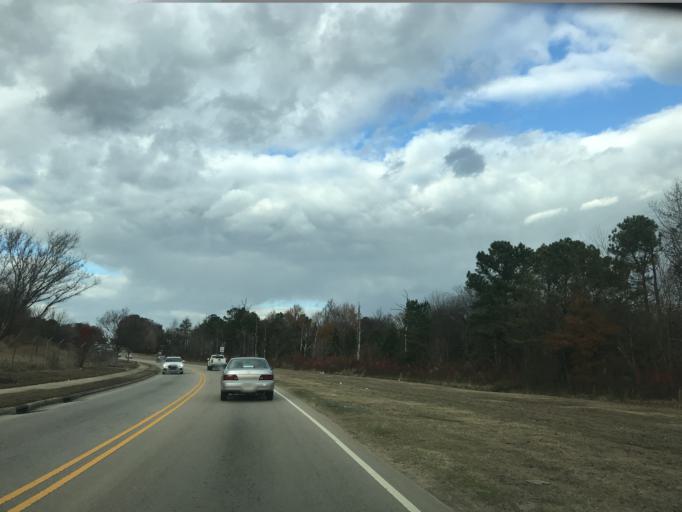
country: US
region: North Carolina
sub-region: Wake County
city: Raleigh
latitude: 35.7893
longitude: -78.5605
